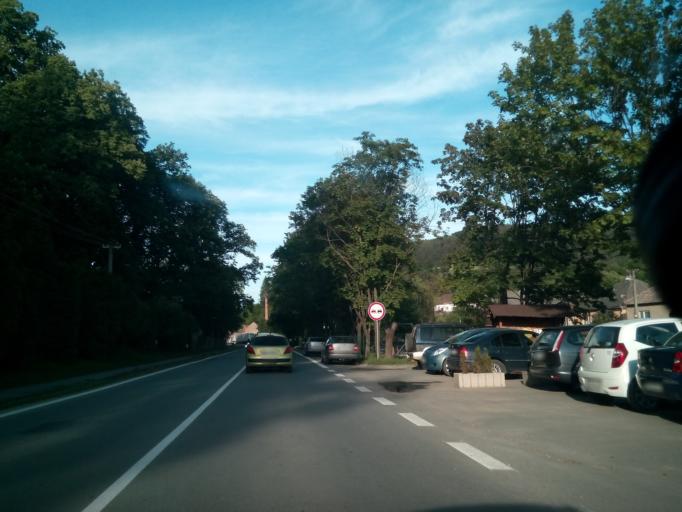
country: SK
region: Presovsky
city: Lipany
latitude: 49.0161
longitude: 20.9719
